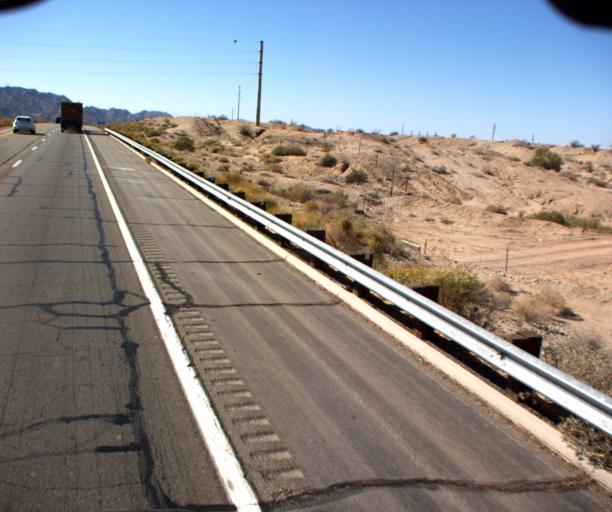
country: US
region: Arizona
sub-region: Yuma County
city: Wellton
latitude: 32.6612
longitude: -114.2591
